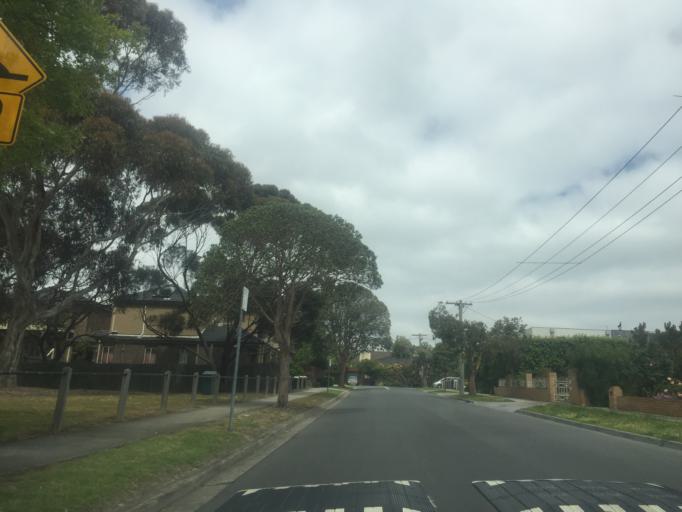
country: AU
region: Victoria
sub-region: Boroondara
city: Kew East
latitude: -37.7995
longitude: 145.0691
